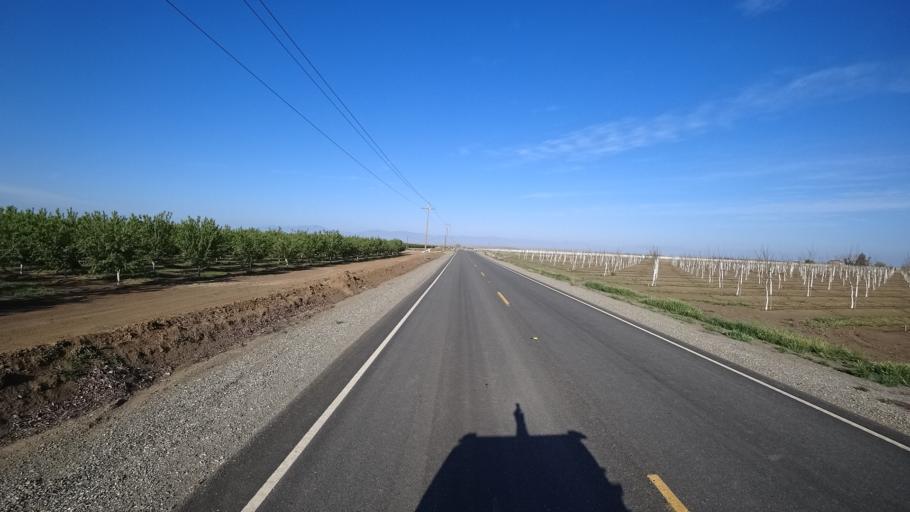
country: US
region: California
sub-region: Glenn County
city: Willows
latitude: 39.5823
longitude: -122.2336
